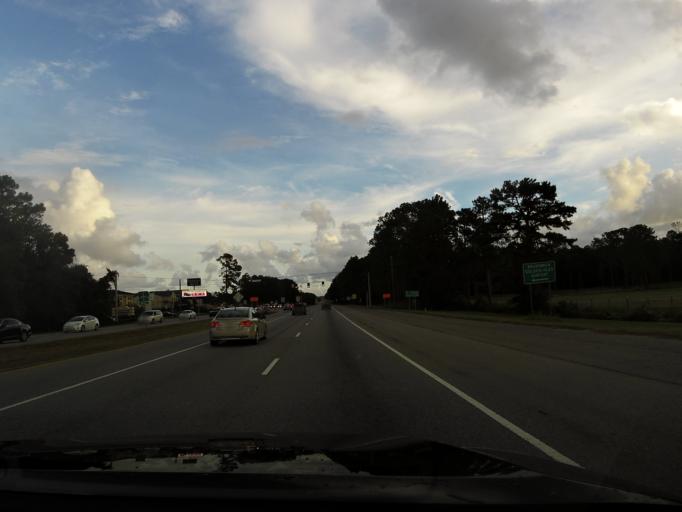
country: US
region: Georgia
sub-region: Glynn County
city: Dock Junction
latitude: 31.2382
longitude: -81.5017
